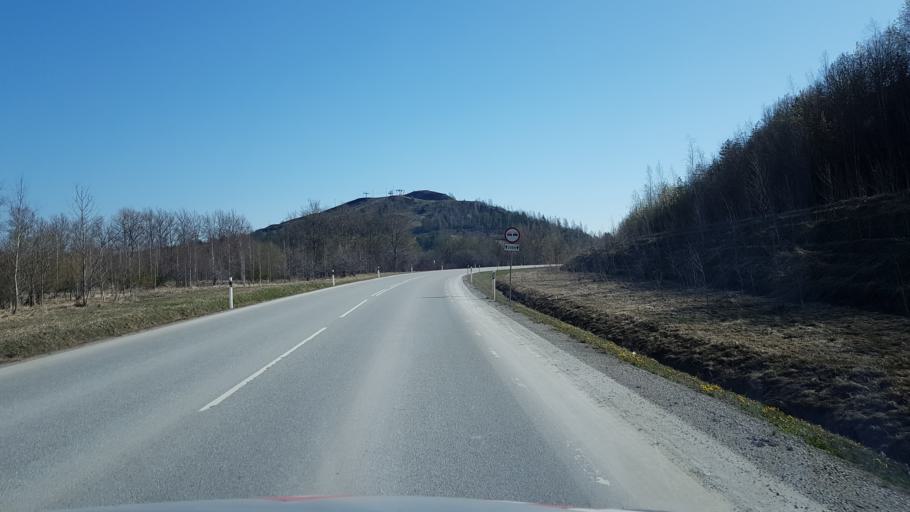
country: EE
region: Ida-Virumaa
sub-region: Kivioli linn
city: Kivioli
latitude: 59.3581
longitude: 26.9396
